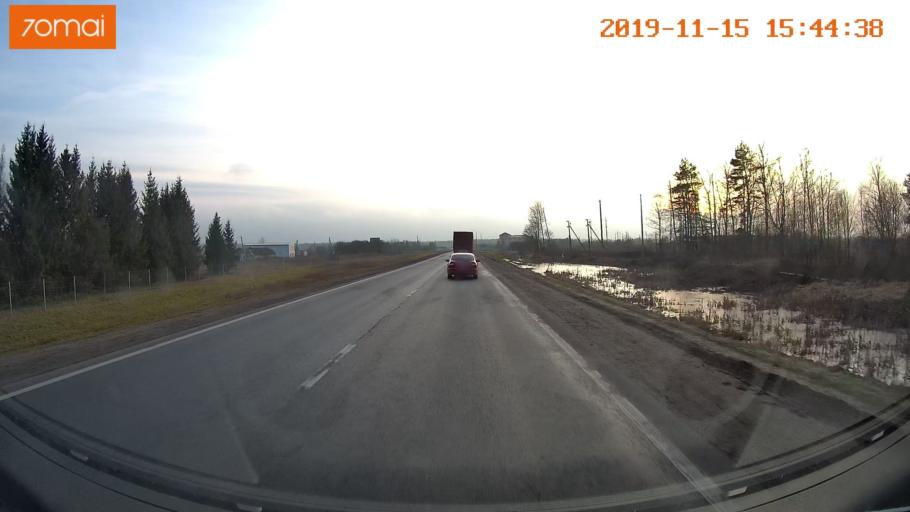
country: RU
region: Jaroslavl
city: Danilov
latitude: 57.9682
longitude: 40.0203
